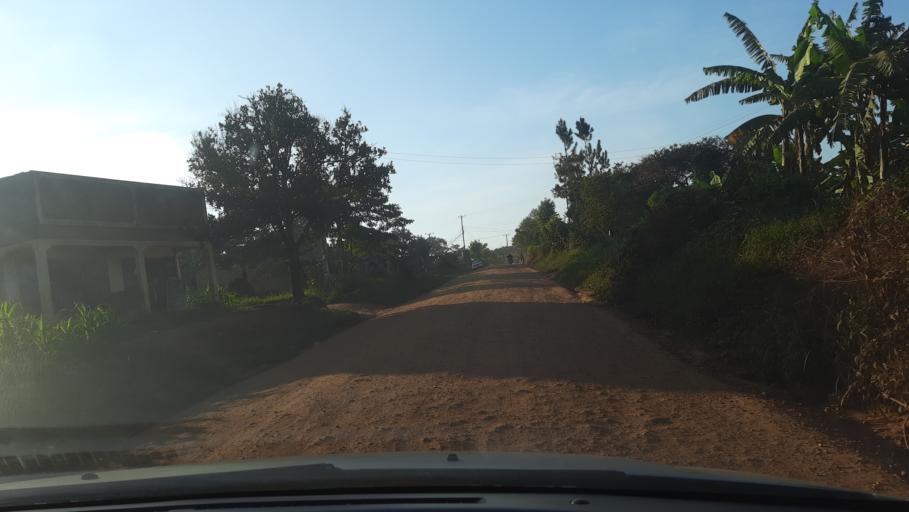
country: UG
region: Central Region
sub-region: Mukono District
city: Mukono
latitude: 0.3719
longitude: 32.7492
